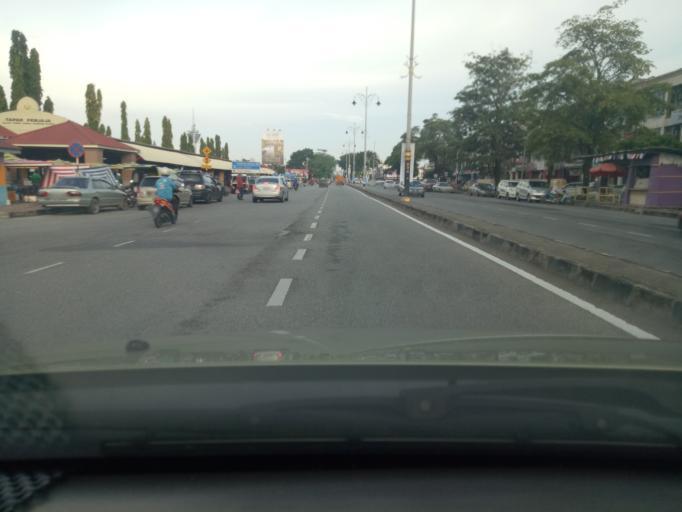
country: MY
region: Kedah
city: Alor Setar
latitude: 6.1258
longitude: 100.3559
